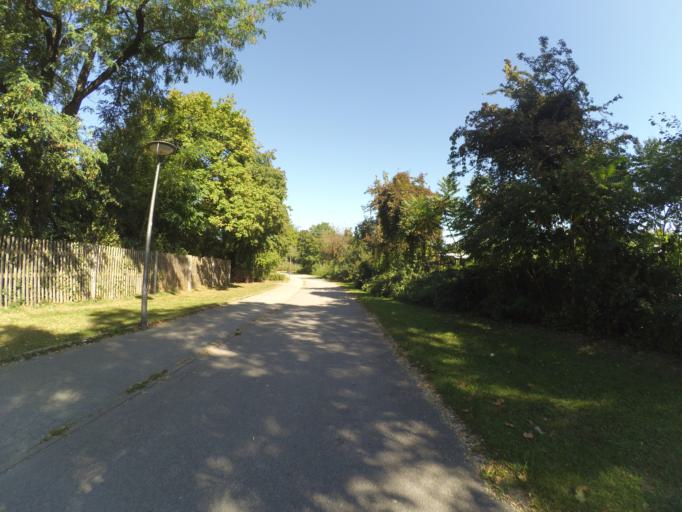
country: DE
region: Bavaria
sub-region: Upper Bavaria
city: Oberschleissheim
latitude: 48.2091
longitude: 11.5724
